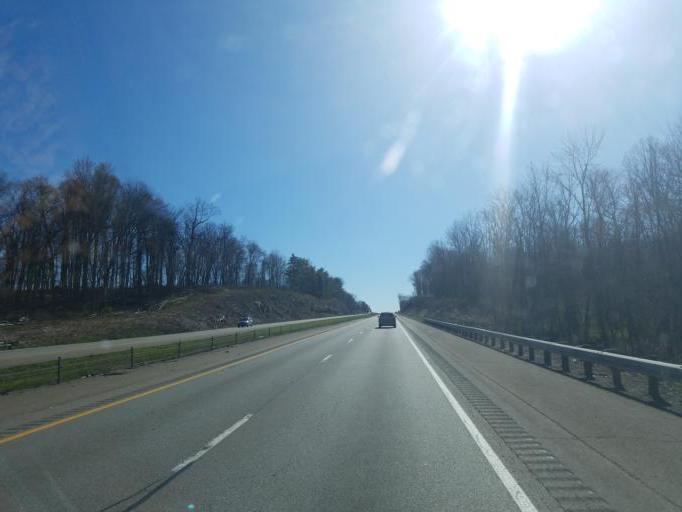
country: US
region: Ohio
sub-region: Perry County
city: Thornport
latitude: 39.9388
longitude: -82.3183
